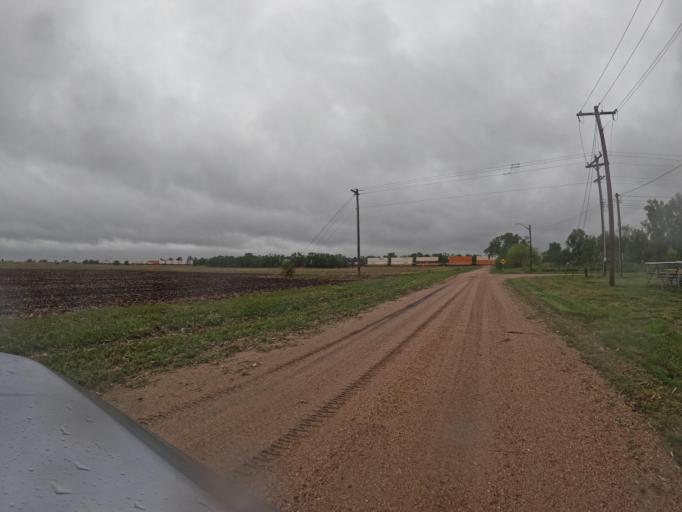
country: US
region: Nebraska
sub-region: Clay County
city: Harvard
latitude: 40.6150
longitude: -98.1027
